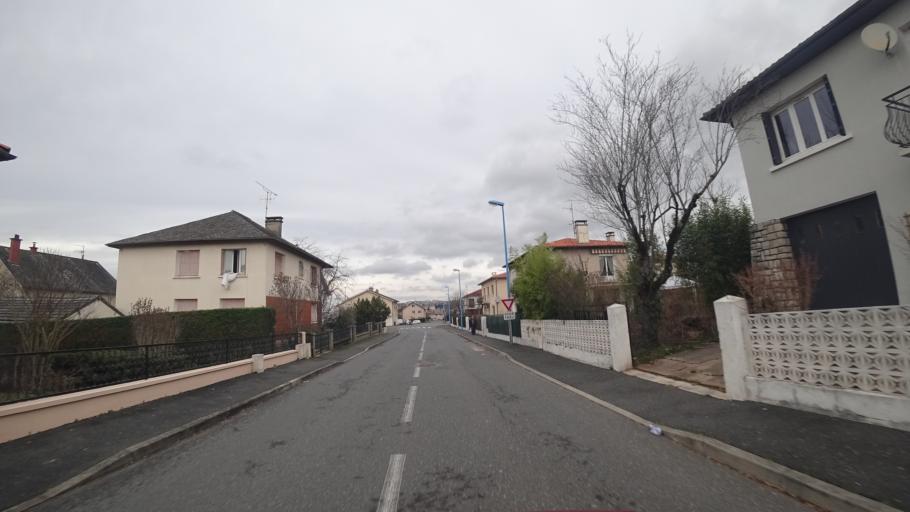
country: FR
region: Midi-Pyrenees
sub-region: Departement de l'Aveyron
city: Rodez
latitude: 44.3670
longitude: 2.5964
